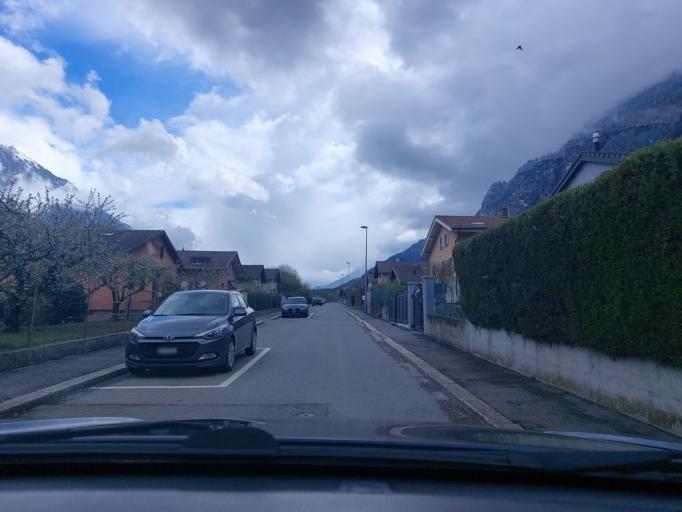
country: CH
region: Valais
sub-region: Saint-Maurice District
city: Saint-Maurice
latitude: 46.2119
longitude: 7.0014
